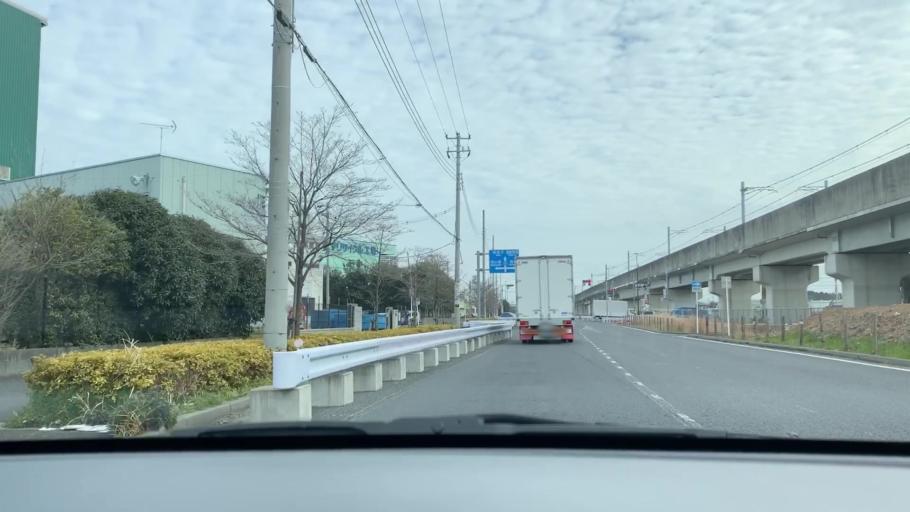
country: JP
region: Chiba
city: Kashiwa
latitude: 35.8848
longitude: 139.9433
